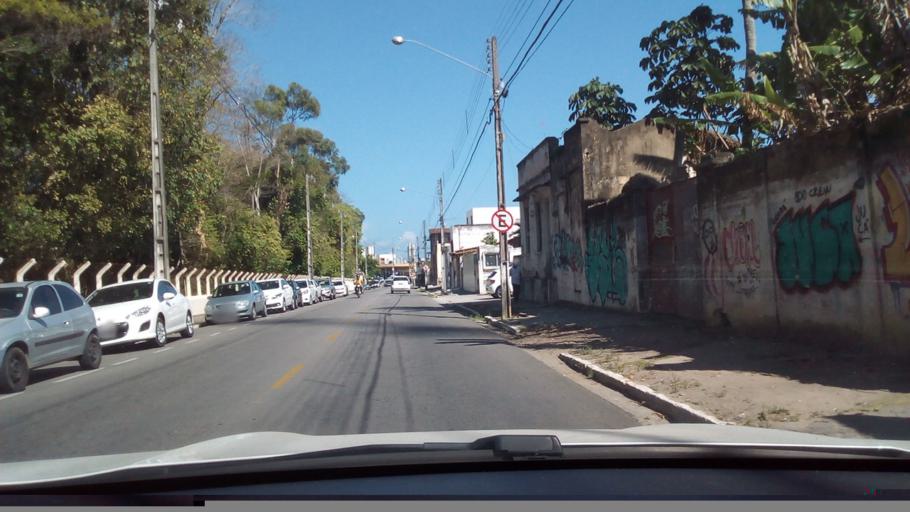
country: BR
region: Paraiba
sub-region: Joao Pessoa
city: Joao Pessoa
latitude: -7.1149
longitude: -34.8765
